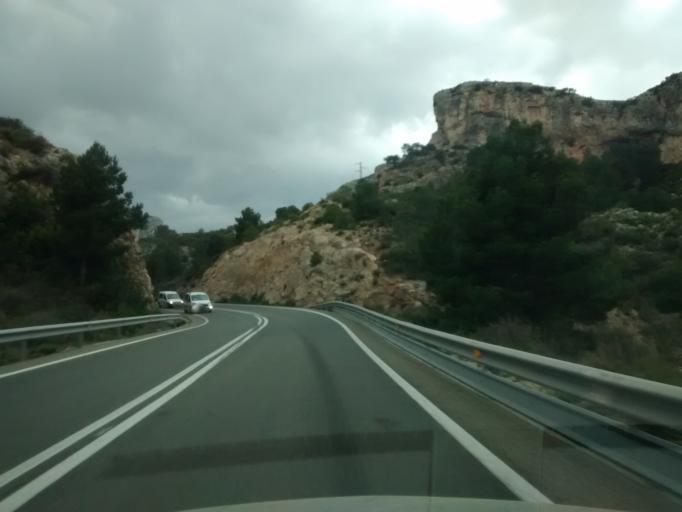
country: ES
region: Catalonia
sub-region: Provincia de Tarragona
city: Gandesa
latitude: 41.0381
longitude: 0.4903
